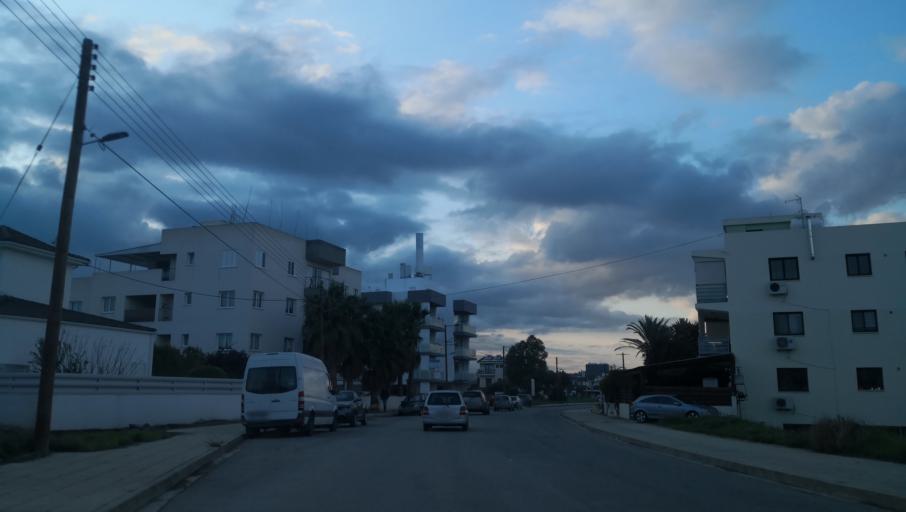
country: CY
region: Lefkosia
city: Kato Deftera
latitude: 35.0985
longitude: 33.3022
